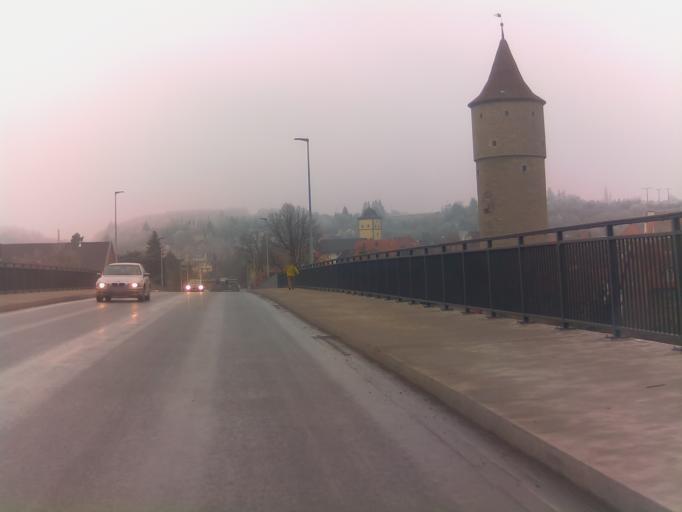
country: DE
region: Bavaria
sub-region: Regierungsbezirk Unterfranken
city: Ochsenfurt
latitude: 49.6675
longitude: 10.0668
